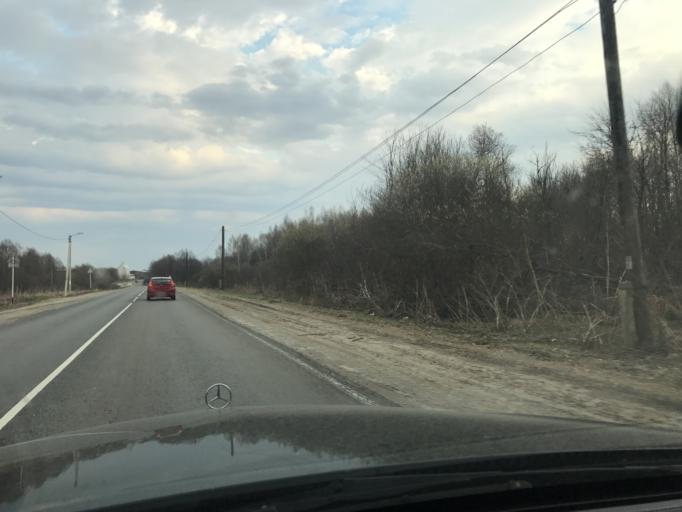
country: RU
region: Vladimir
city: Krasnaya Gorbatka
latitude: 55.6558
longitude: 41.8185
